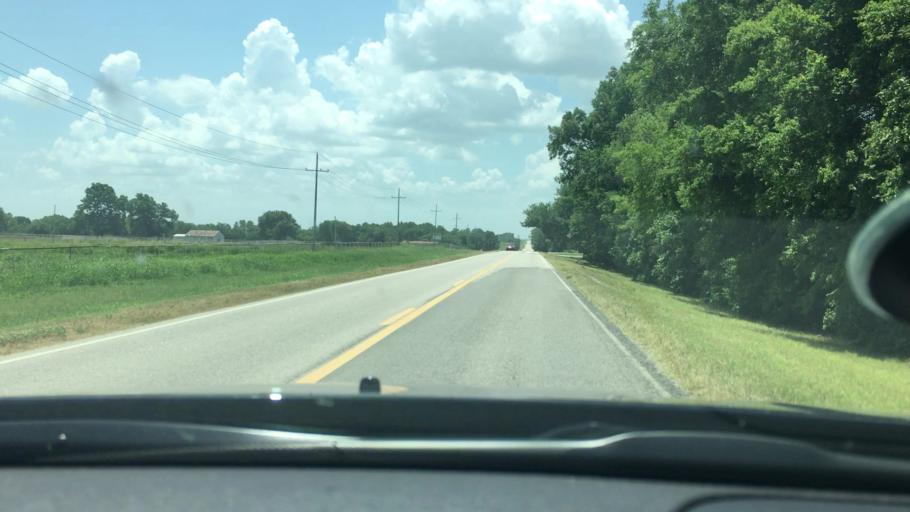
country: US
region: Oklahoma
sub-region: Pontotoc County
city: Ada
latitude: 34.6920
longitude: -96.6349
